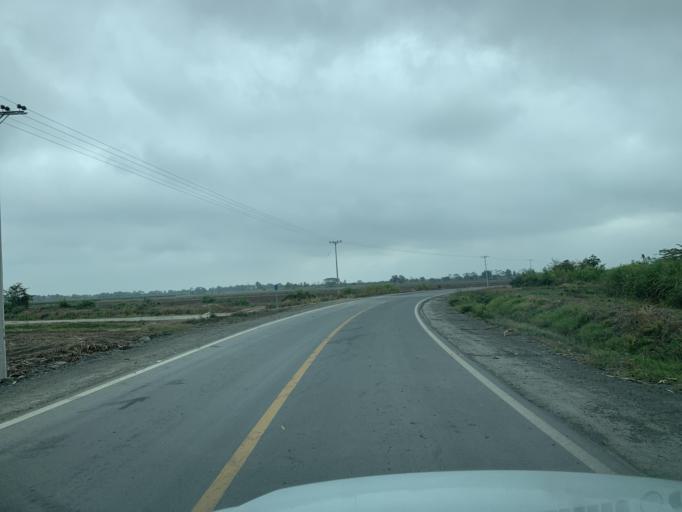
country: EC
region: Guayas
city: Coronel Marcelino Mariduena
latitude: -2.3087
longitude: -79.5095
